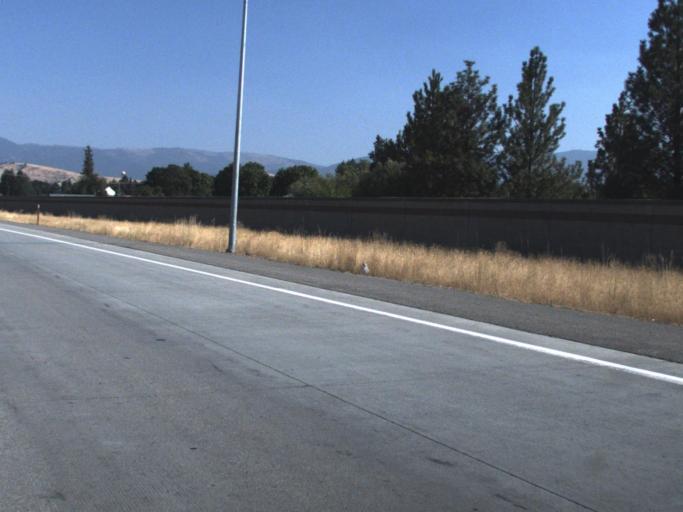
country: US
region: Washington
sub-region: Spokane County
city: Veradale
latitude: 47.6660
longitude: -117.1811
